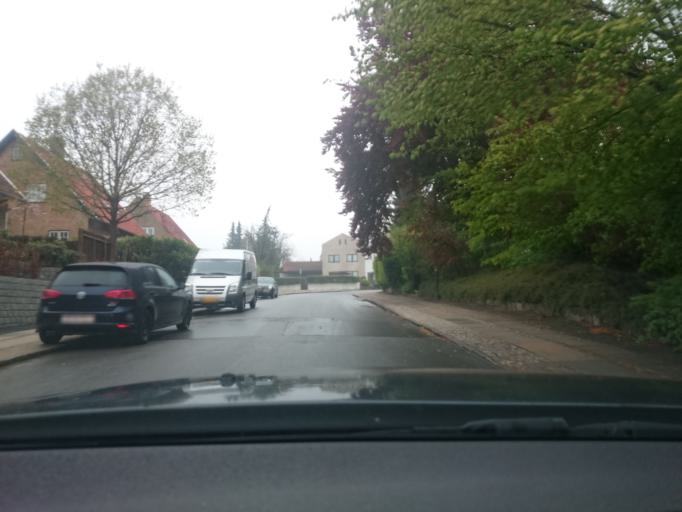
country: DK
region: Capital Region
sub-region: Gentofte Kommune
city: Charlottenlund
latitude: 55.7522
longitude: 12.5521
